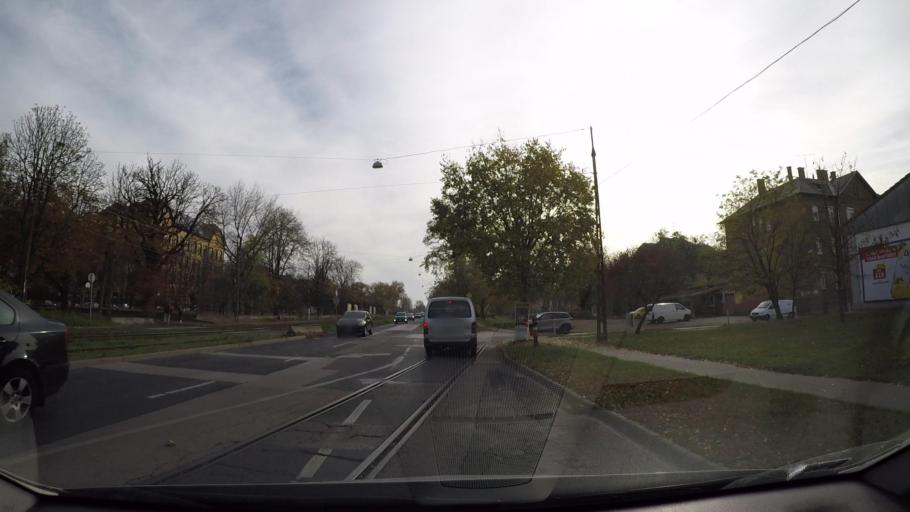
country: HU
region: Budapest
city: Budapest X. keruelet
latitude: 47.4863
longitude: 19.1538
